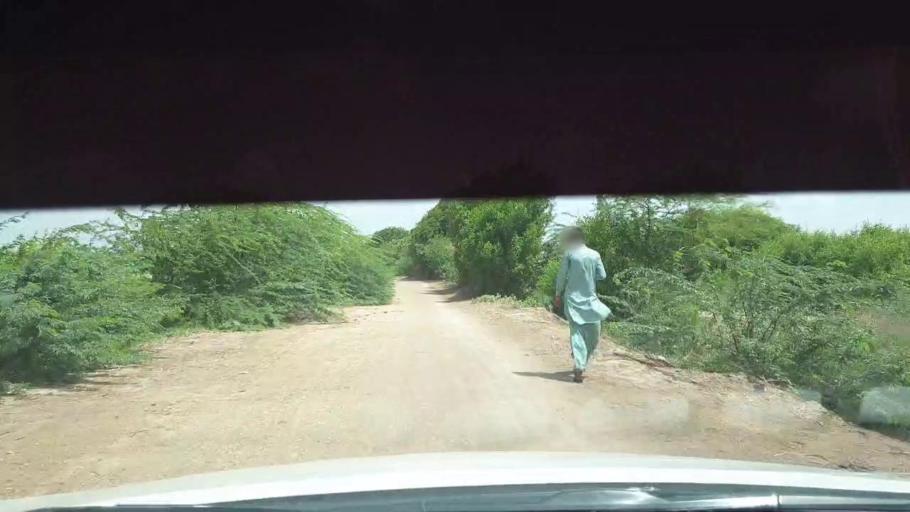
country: PK
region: Sindh
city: Kadhan
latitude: 24.5119
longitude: 68.9756
